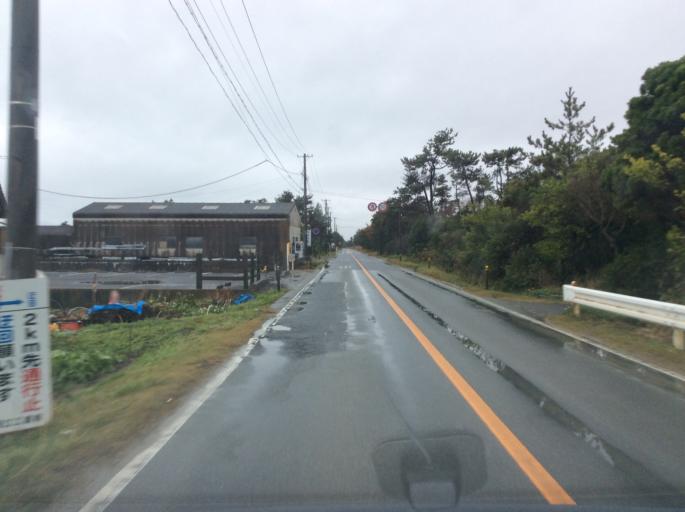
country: JP
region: Fukushima
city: Iwaki
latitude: 37.0814
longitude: 140.9797
